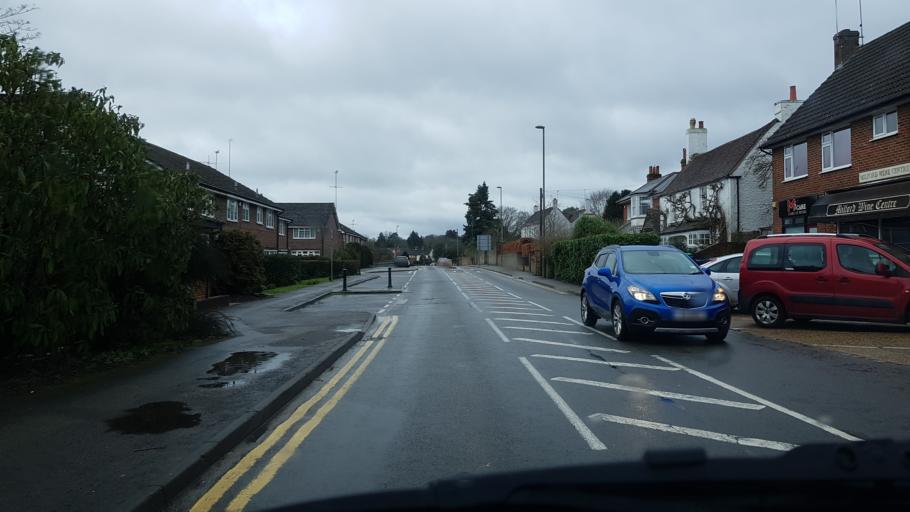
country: GB
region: England
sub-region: Surrey
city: Milford
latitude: 51.1713
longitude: -0.6430
